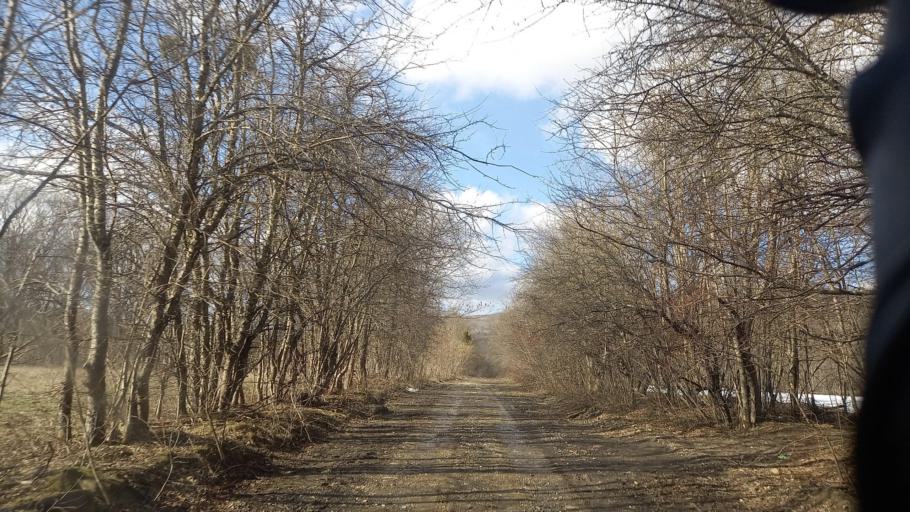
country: RU
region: Krasnodarskiy
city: Smolenskaya
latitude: 44.5958
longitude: 38.8829
